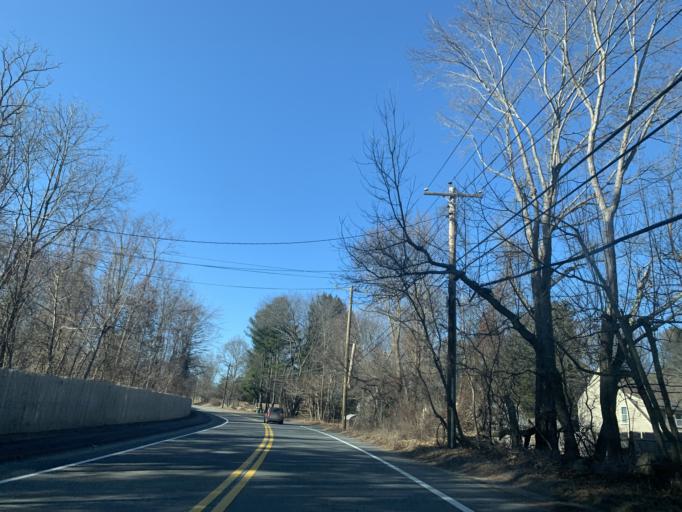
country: US
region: Massachusetts
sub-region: Middlesex County
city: Wayland
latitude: 42.3622
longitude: -71.3483
